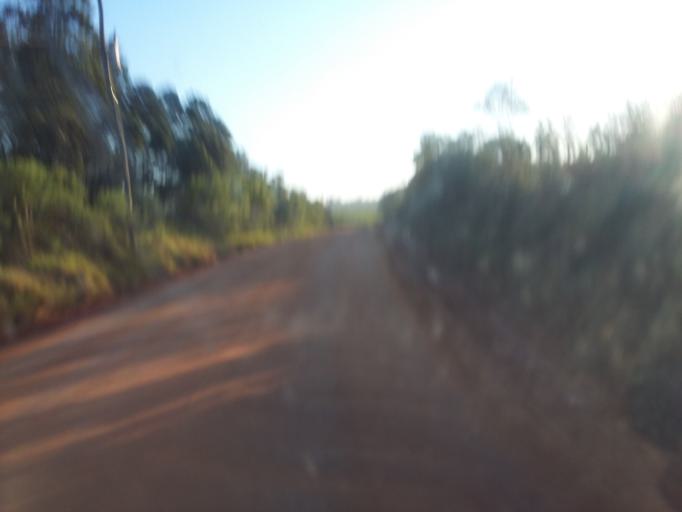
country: BR
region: Rio Grande do Sul
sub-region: Camaqua
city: Camaqua
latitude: -30.7590
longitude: -51.7789
